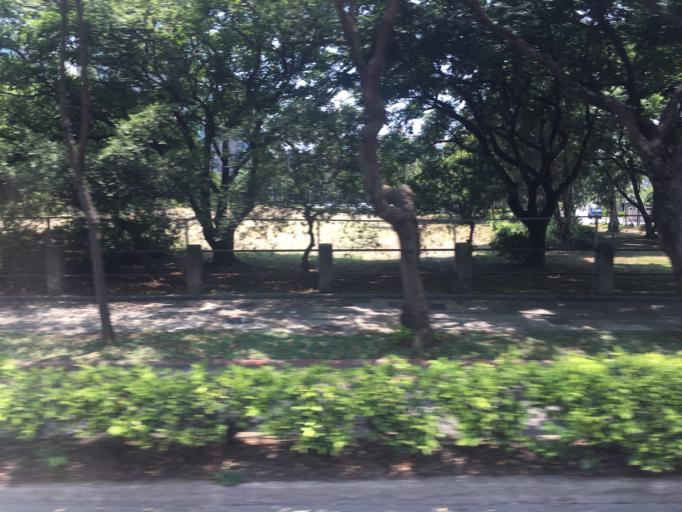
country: TW
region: Taiwan
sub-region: Hsinchu
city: Hsinchu
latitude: 24.7769
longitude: 121.0090
